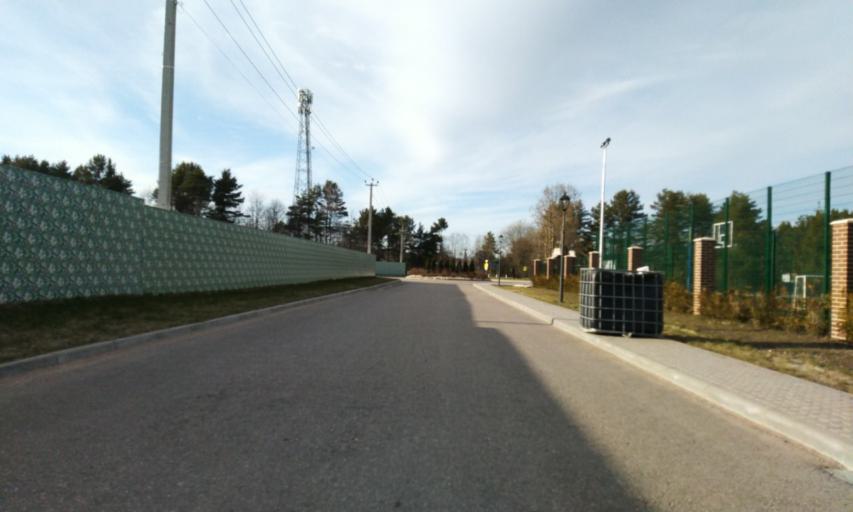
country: RU
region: Leningrad
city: Novoye Devyatkino
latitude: 60.1101
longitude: 30.4462
